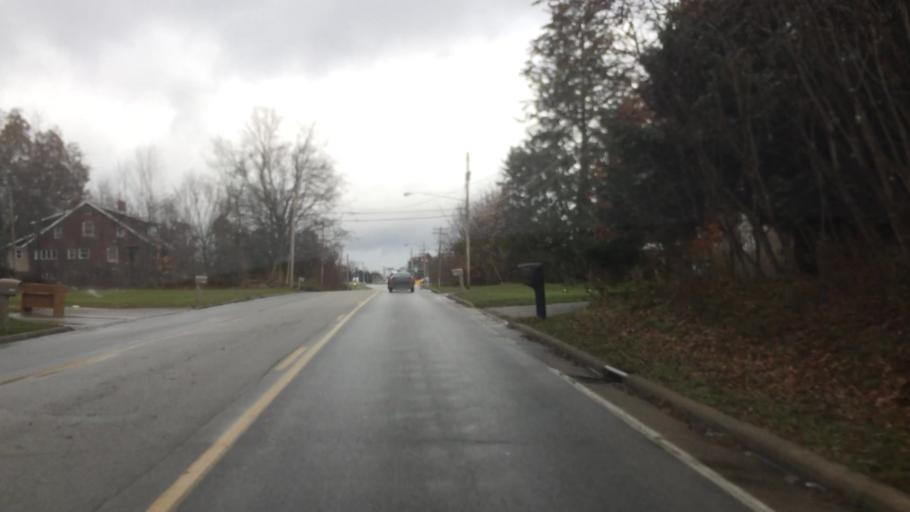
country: US
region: Ohio
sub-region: Summit County
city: Silver Lake
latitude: 41.1788
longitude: -81.4756
